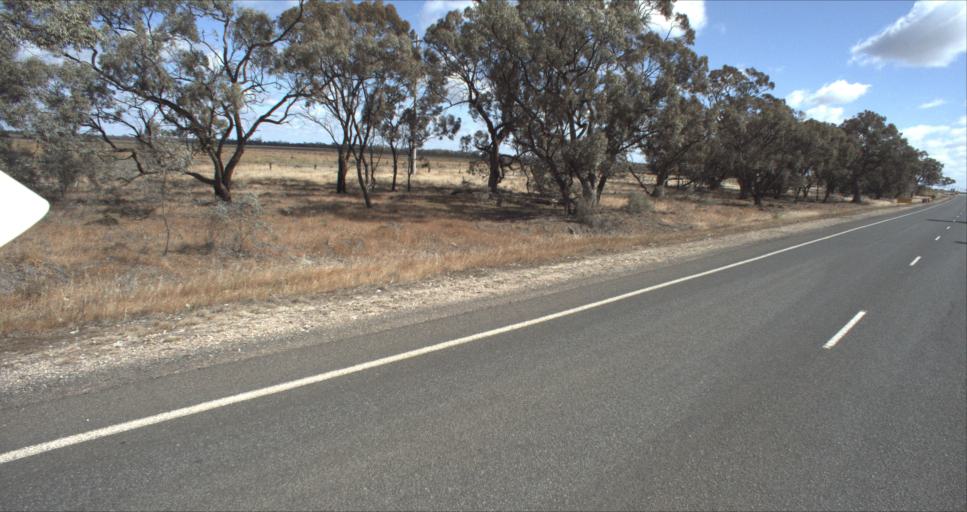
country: AU
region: New South Wales
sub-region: Murrumbidgee Shire
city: Darlington Point
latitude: -34.5567
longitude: 146.1698
